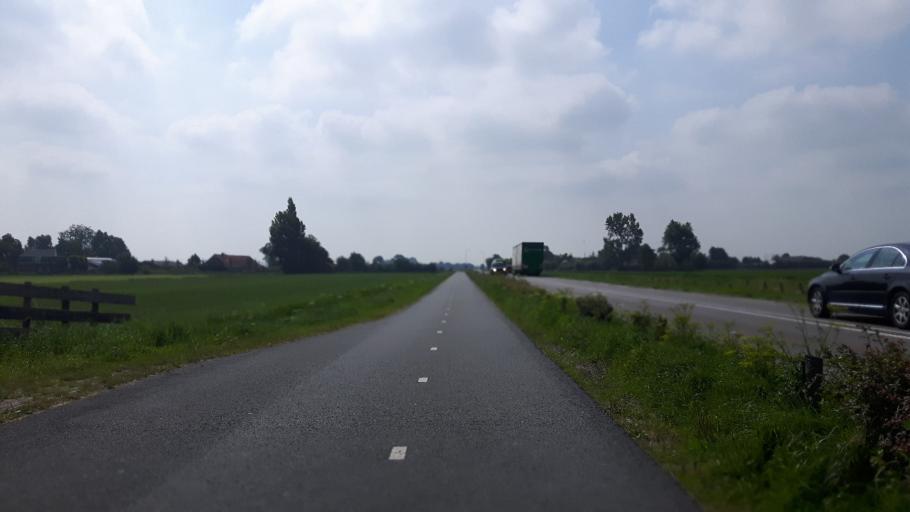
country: NL
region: Utrecht
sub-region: Gemeente Montfoort
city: Montfoort
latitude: 52.0285
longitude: 4.9440
